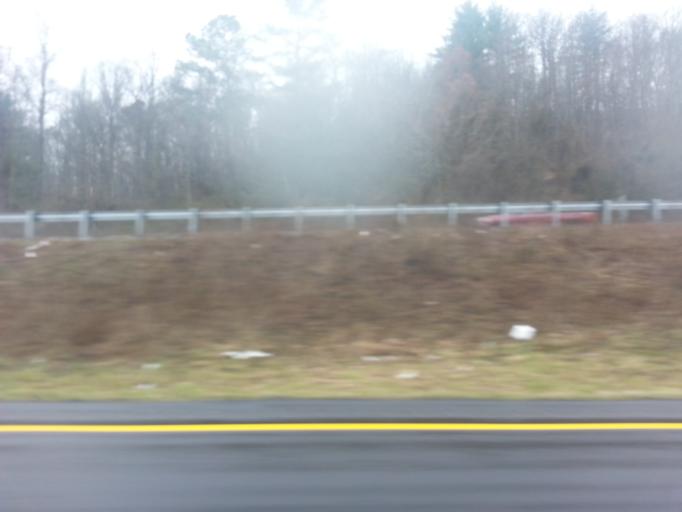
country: US
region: Tennessee
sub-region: Roane County
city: Midtown
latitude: 35.9055
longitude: -84.5748
